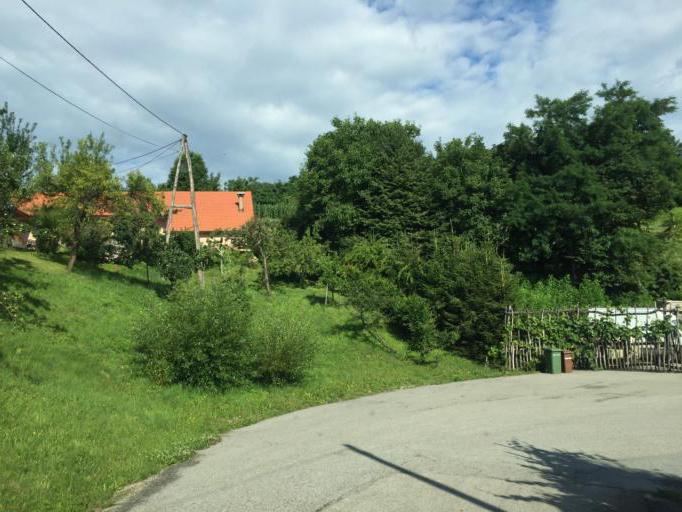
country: AT
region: Styria
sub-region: Politischer Bezirk Suedoststeiermark
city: Bad Radkersburg
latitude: 46.6736
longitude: 15.9637
